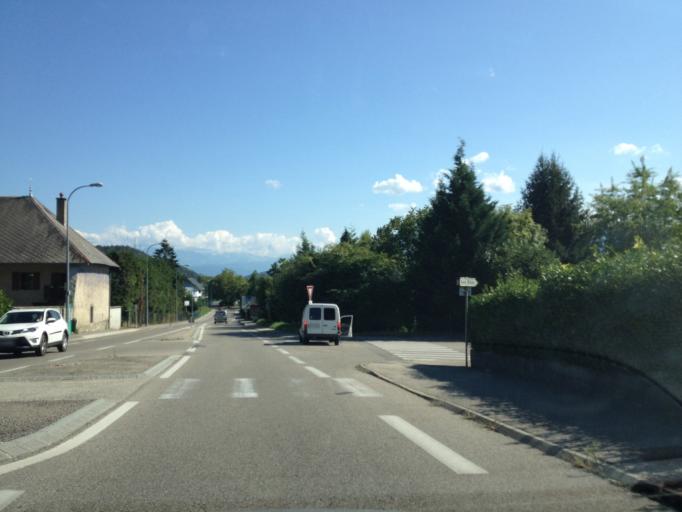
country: FR
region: Rhone-Alpes
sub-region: Departement de la Savoie
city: Sonnaz
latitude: 45.6041
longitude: 5.9128
